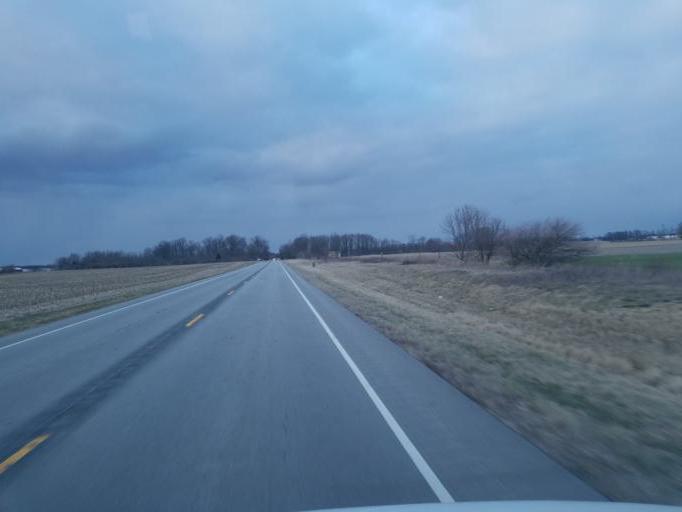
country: US
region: Indiana
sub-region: Henry County
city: Knightstown
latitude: 39.8194
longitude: -85.4343
